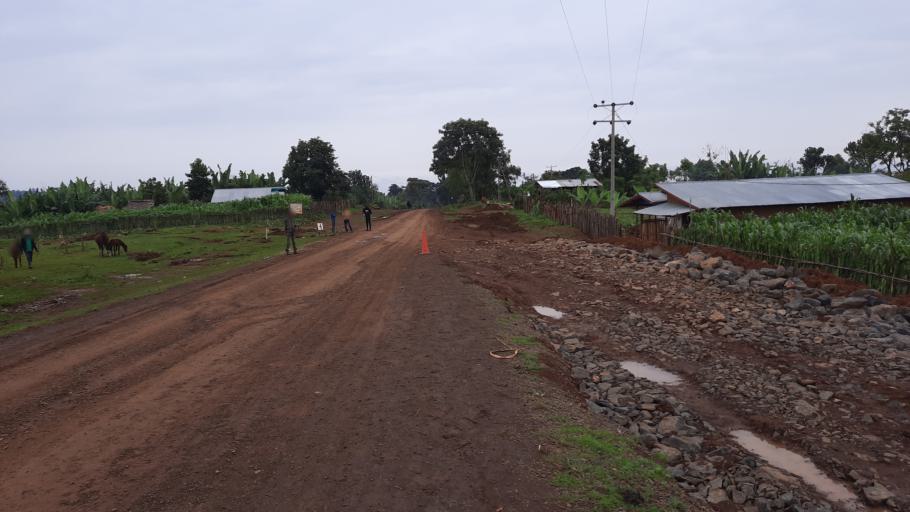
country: ET
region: Oromiya
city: Gore
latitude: 7.8067
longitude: 35.4583
